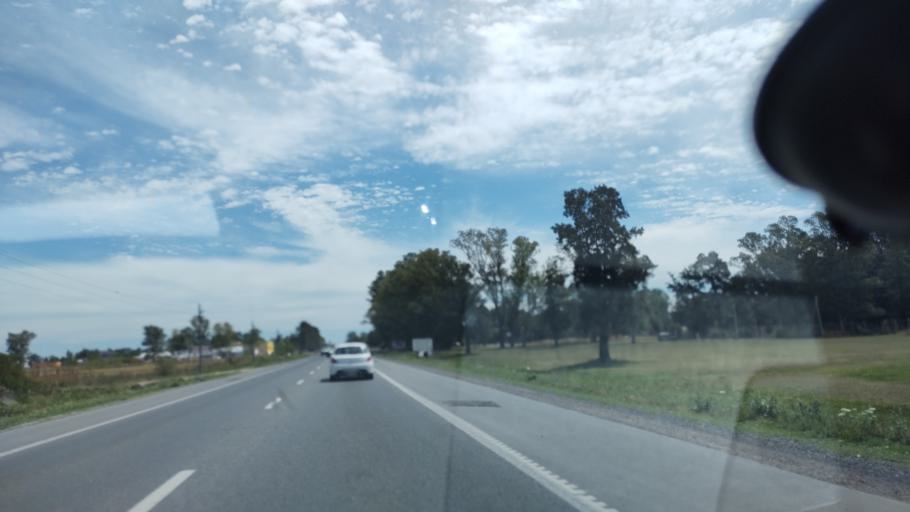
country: AR
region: Buenos Aires
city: Canuelas
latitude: -35.0336
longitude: -58.7535
